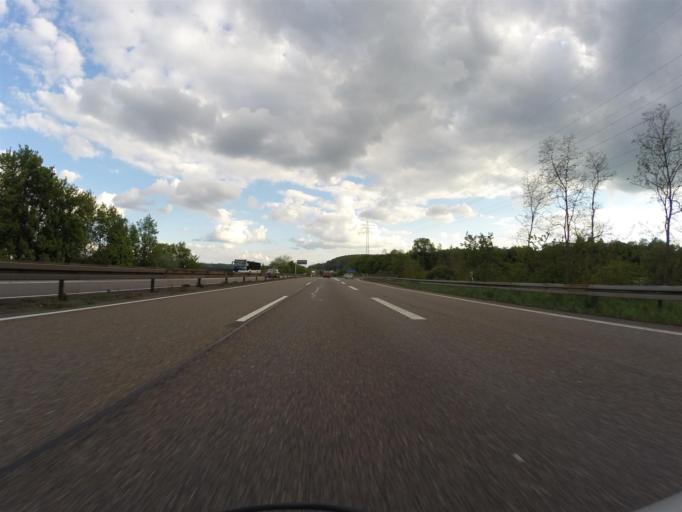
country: DE
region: Saarland
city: Volklingen
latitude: 49.2534
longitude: 6.8331
